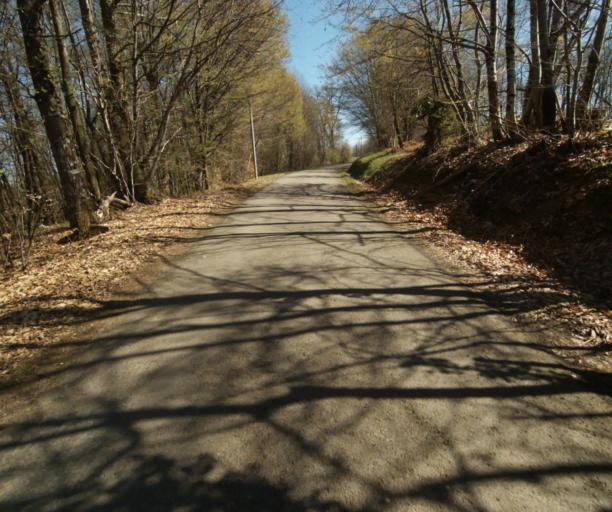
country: FR
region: Limousin
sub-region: Departement de la Correze
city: Chameyrat
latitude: 45.2525
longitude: 1.7095
